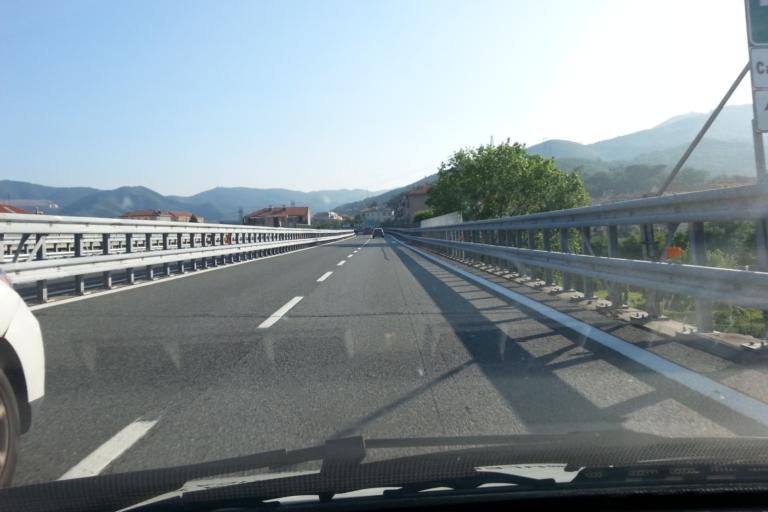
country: IT
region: Liguria
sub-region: Provincia di Savona
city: Valleggia
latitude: 44.2835
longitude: 8.4322
